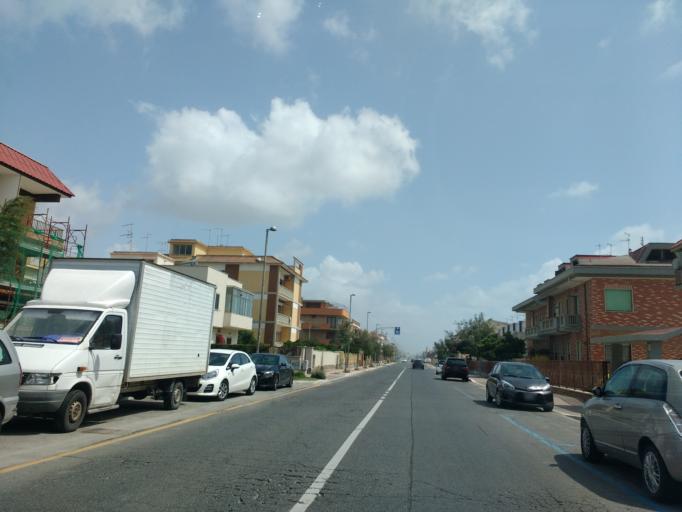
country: IT
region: Latium
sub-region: Citta metropolitana di Roma Capitale
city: Torvaianica
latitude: 41.6157
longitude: 12.4681
